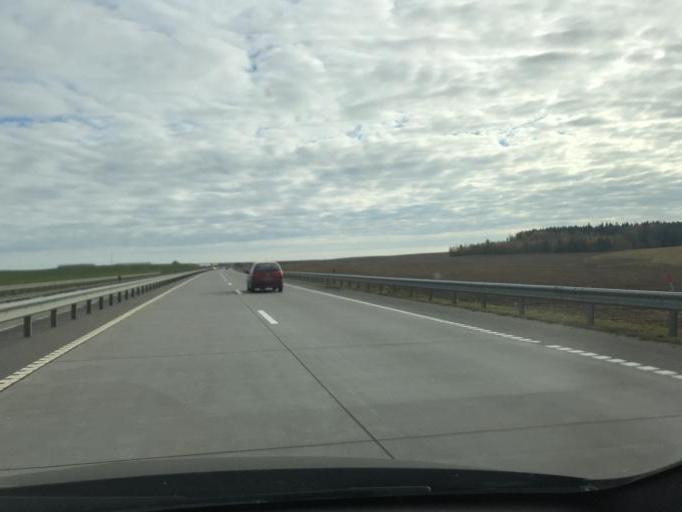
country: BY
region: Minsk
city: Syomkava
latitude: 54.0661
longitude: 27.4841
